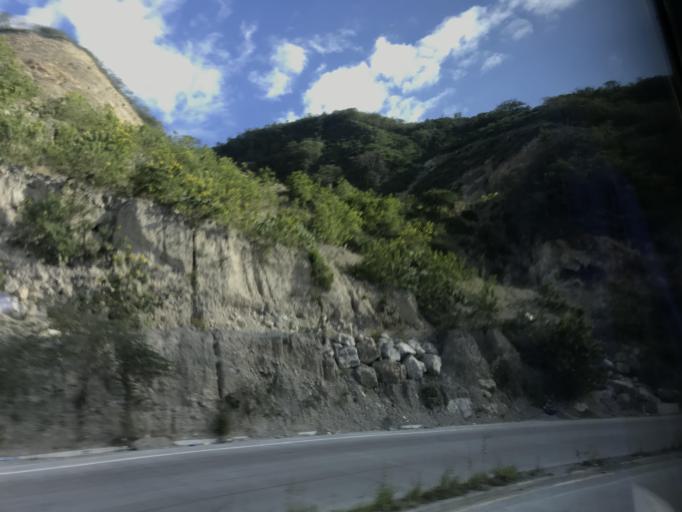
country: GT
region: El Progreso
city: Guastatoya
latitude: 14.8459
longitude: -90.1261
